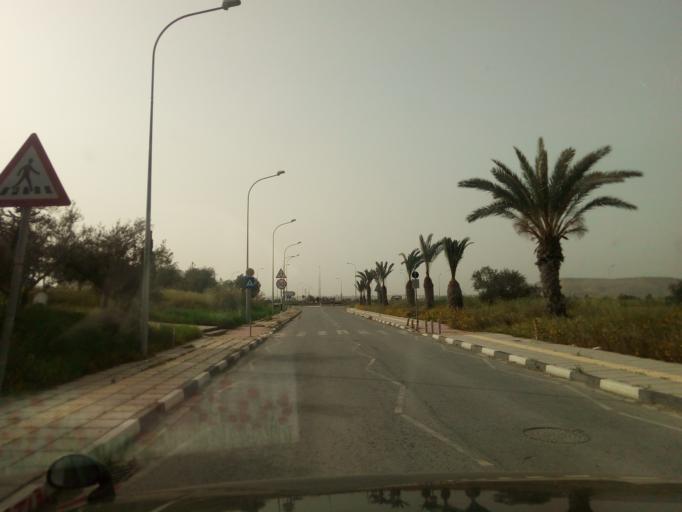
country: CY
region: Larnaka
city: Athienou
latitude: 35.0580
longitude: 33.5244
